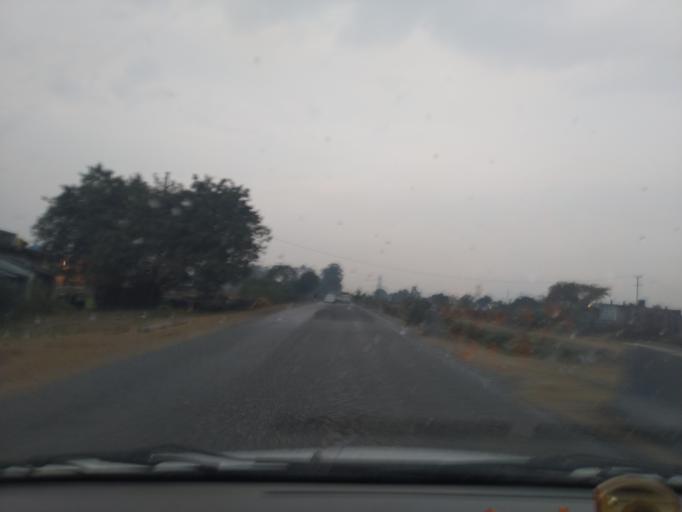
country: IN
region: Bihar
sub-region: Kaimur District
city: Bhabua
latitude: 25.1092
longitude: 83.7001
